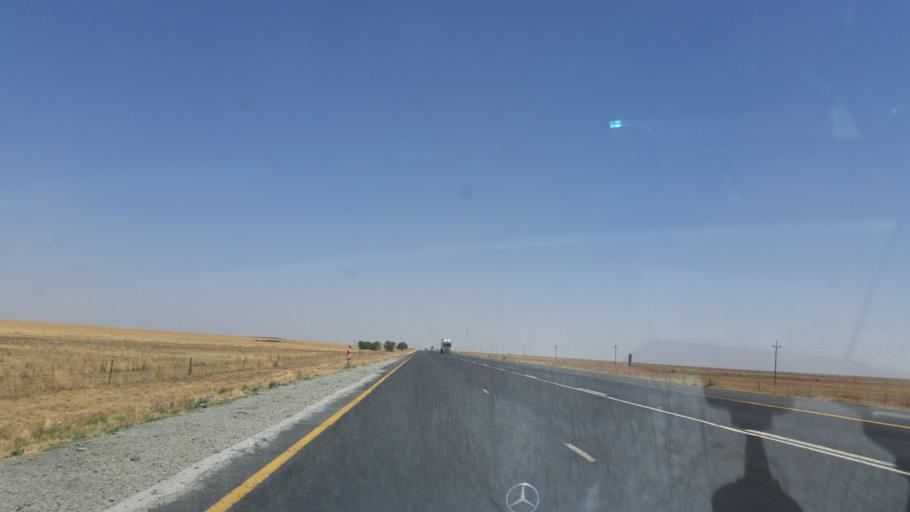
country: ZA
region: Orange Free State
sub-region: Lejweleputswa District Municipality
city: Brandfort
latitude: -28.8036
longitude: 26.6843
